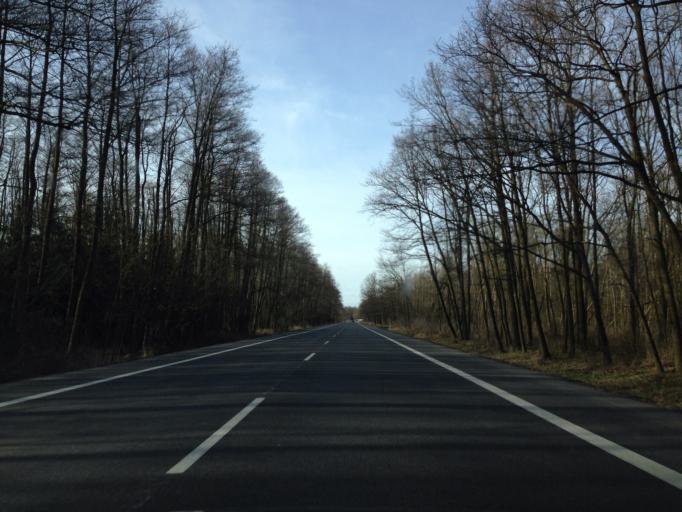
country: PL
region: Lodz Voivodeship
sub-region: Powiat kutnowski
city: Ostrowy
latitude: 52.3467
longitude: 19.1462
